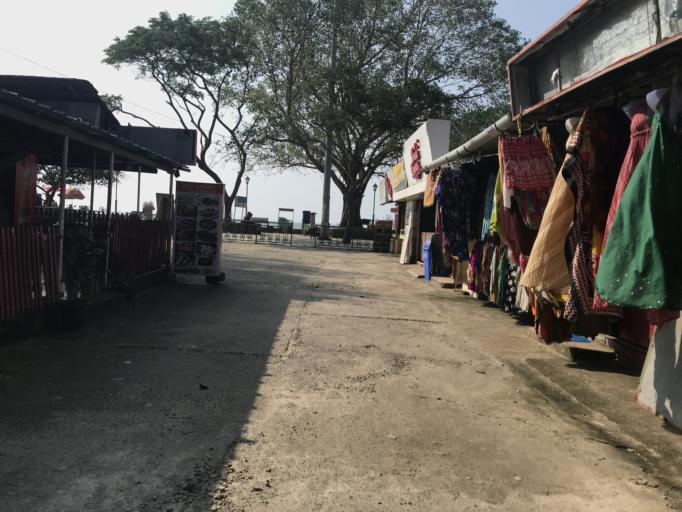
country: IN
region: Kerala
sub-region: Ernakulam
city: Cochin
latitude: 9.9653
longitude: 76.2385
